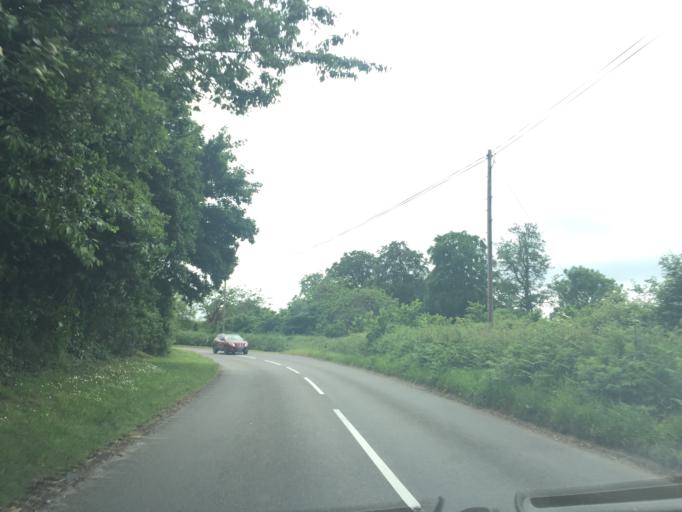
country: GB
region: England
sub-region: Dorset
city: Wareham
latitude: 50.6734
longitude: -2.1615
